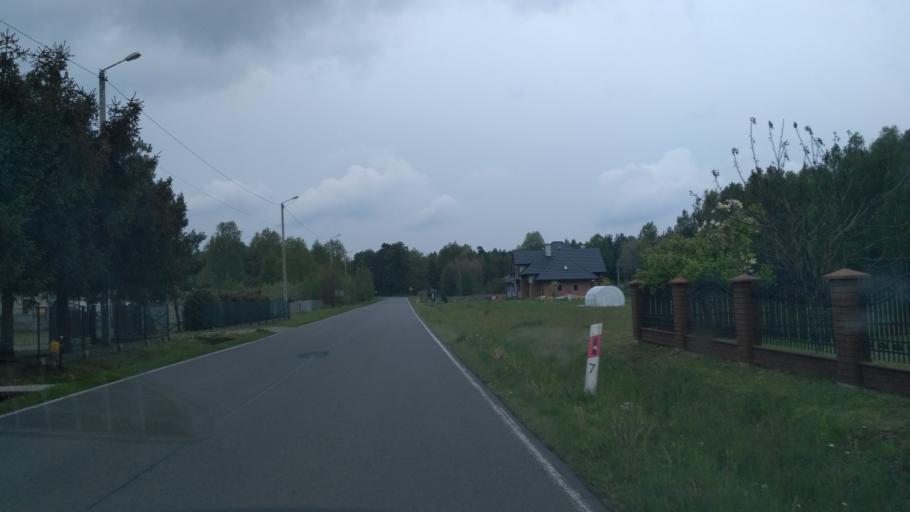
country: PL
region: Subcarpathian Voivodeship
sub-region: Powiat kolbuszowski
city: Kolbuszowa
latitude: 50.1794
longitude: 21.7599
